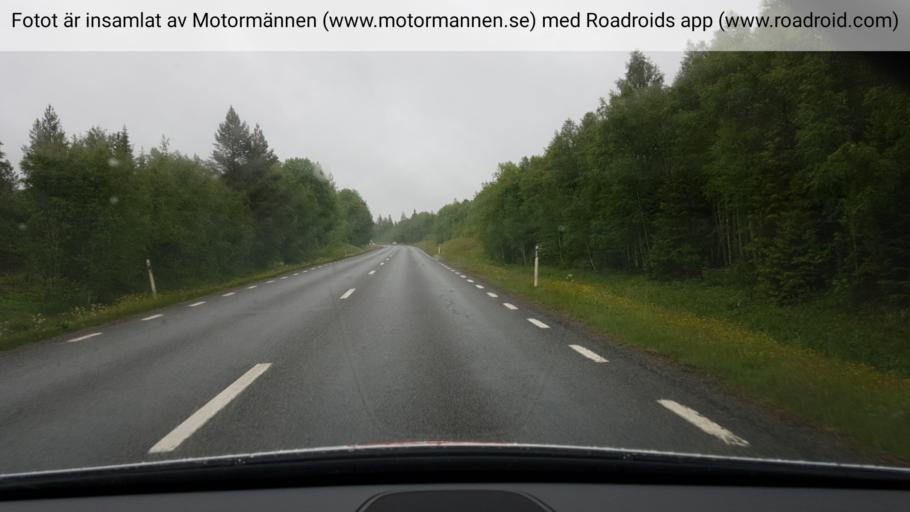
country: SE
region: Jaemtland
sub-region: OEstersunds Kommun
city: Lit
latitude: 63.4162
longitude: 15.0937
